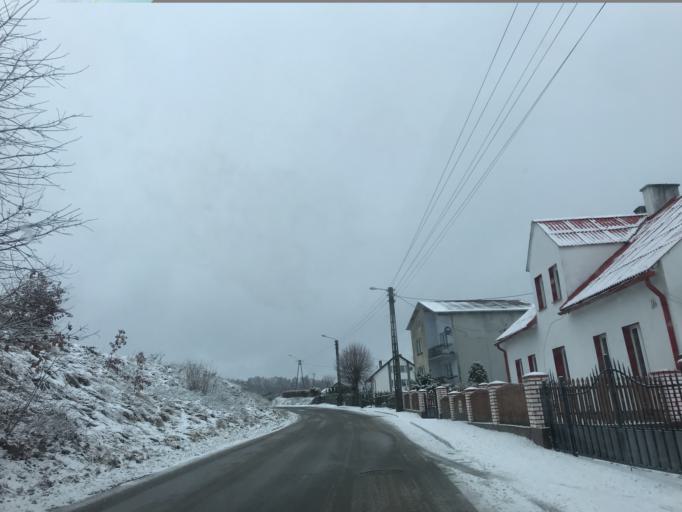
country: PL
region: Pomeranian Voivodeship
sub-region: Powiat bytowski
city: Bytow
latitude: 54.2184
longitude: 17.5624
